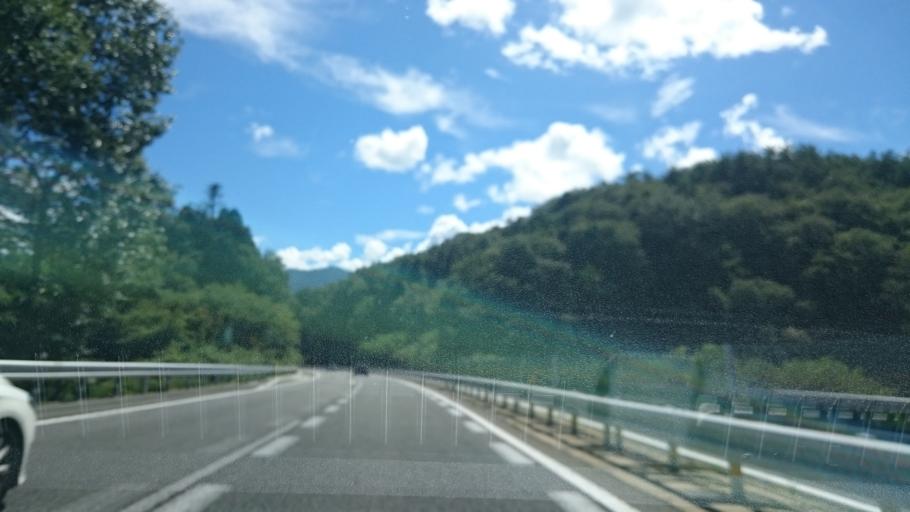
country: JP
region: Nagano
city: Iida
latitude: 35.4572
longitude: 137.7511
